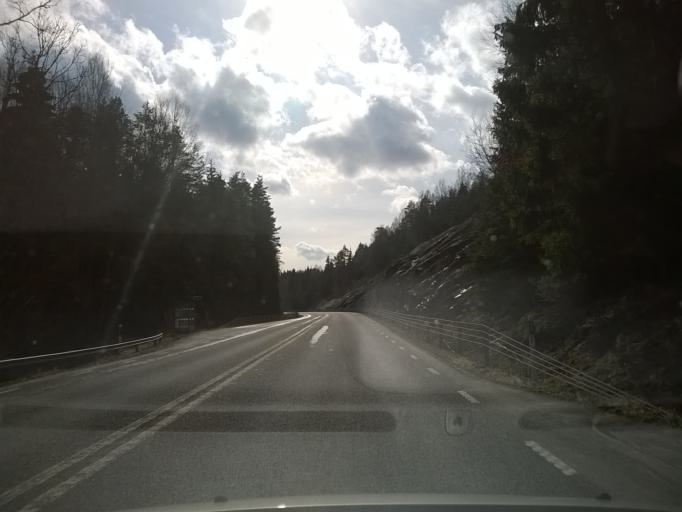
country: SE
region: Vaestra Goetaland
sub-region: Orust
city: Henan
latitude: 58.1944
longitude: 11.6894
